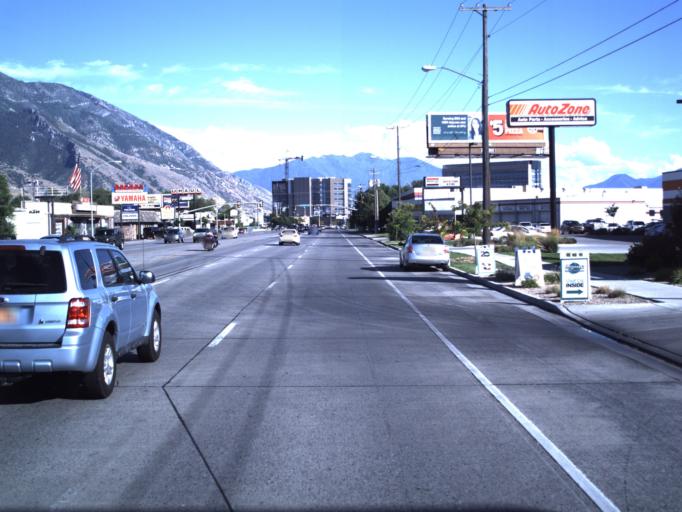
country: US
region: Utah
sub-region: Utah County
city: Provo
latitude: 40.2550
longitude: -111.6713
